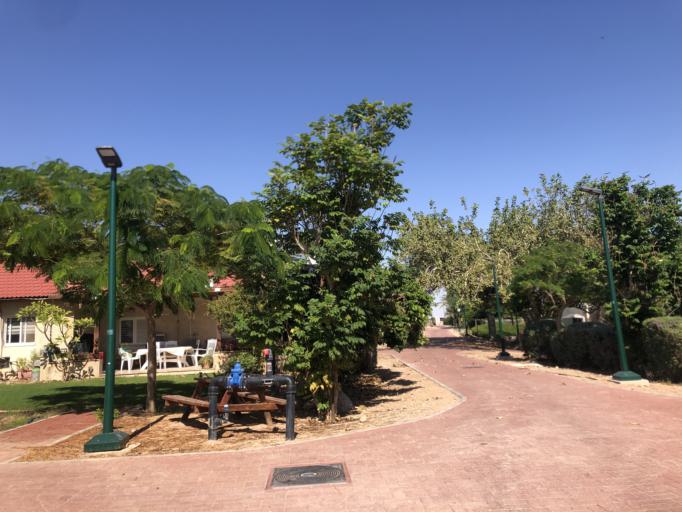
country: IL
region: Southern District
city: Eilat
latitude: 29.5820
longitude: 34.9605
